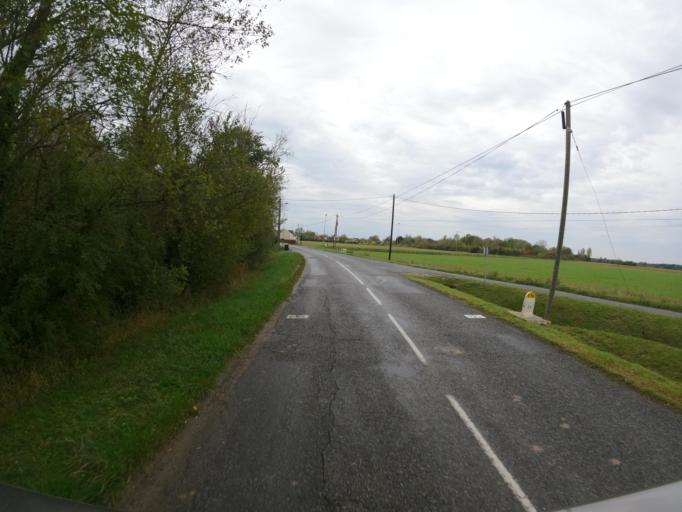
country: FR
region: Ile-de-France
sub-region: Departement de Seine-et-Marne
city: Villeneuve-le-Comte
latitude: 48.8199
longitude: 2.8315
